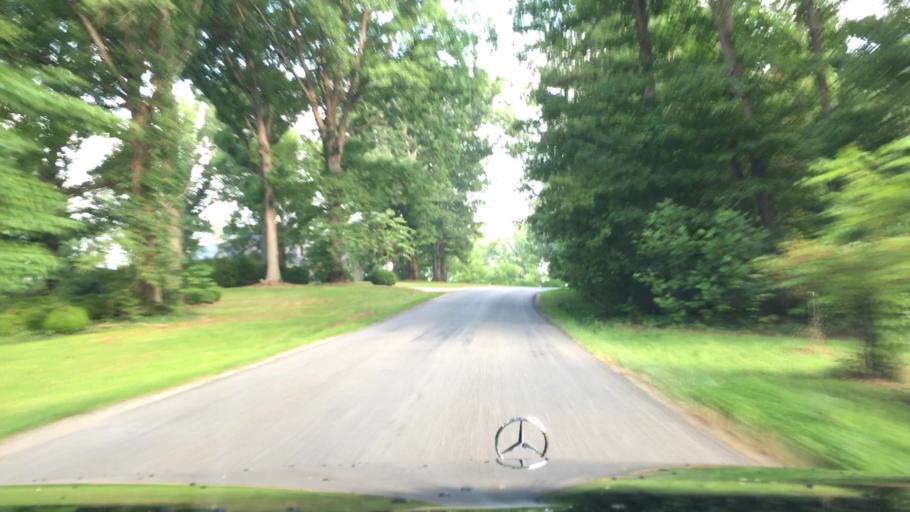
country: US
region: Virginia
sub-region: Campbell County
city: Timberlake
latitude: 37.2509
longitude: -79.3112
